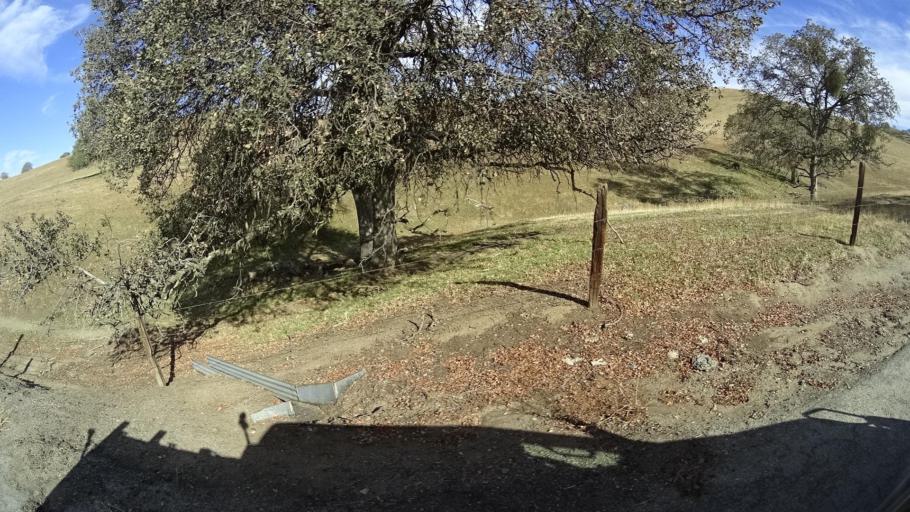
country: US
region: California
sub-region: Kern County
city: Oildale
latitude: 35.5748
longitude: -118.8076
